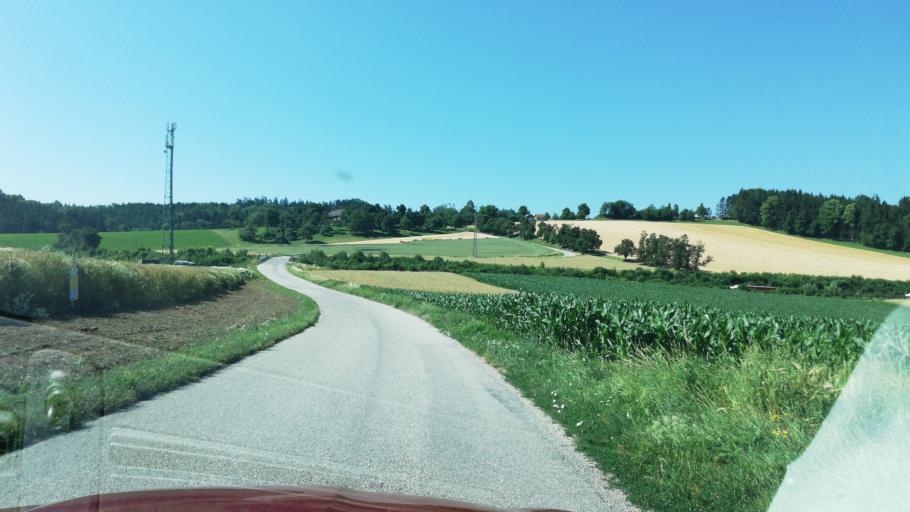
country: AT
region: Upper Austria
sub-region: Politischer Bezirk Grieskirchen
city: Bad Schallerbach
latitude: 48.1898
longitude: 13.9423
